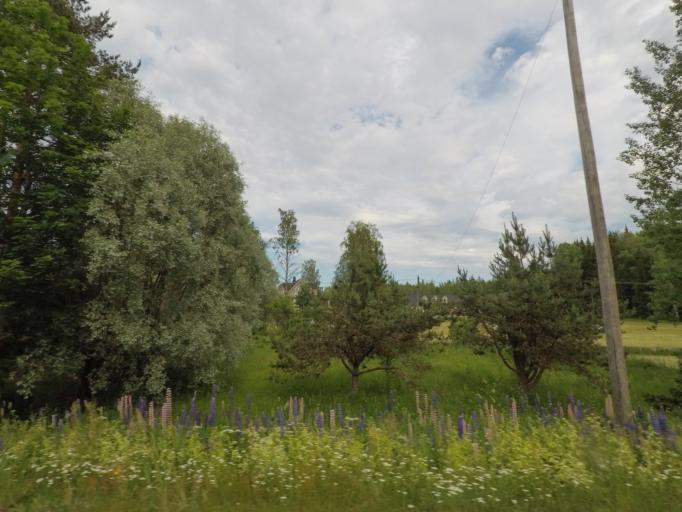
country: FI
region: Paijanne Tavastia
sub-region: Lahti
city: Hollola
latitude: 60.8709
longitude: 25.5019
